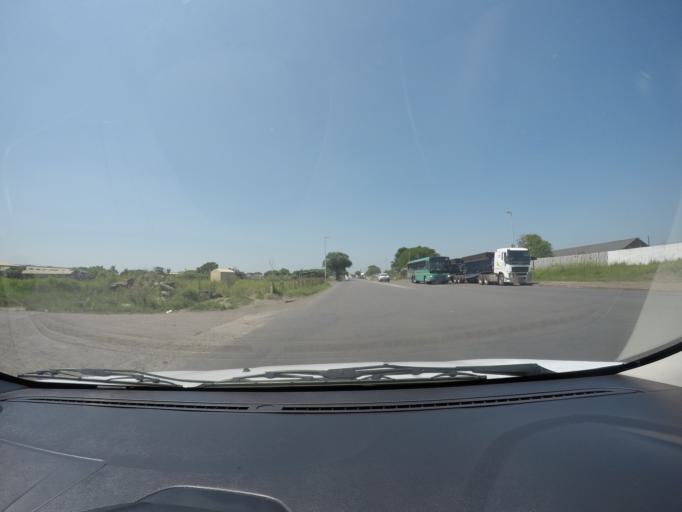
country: ZA
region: KwaZulu-Natal
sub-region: uThungulu District Municipality
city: Richards Bay
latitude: -28.7605
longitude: 32.0236
